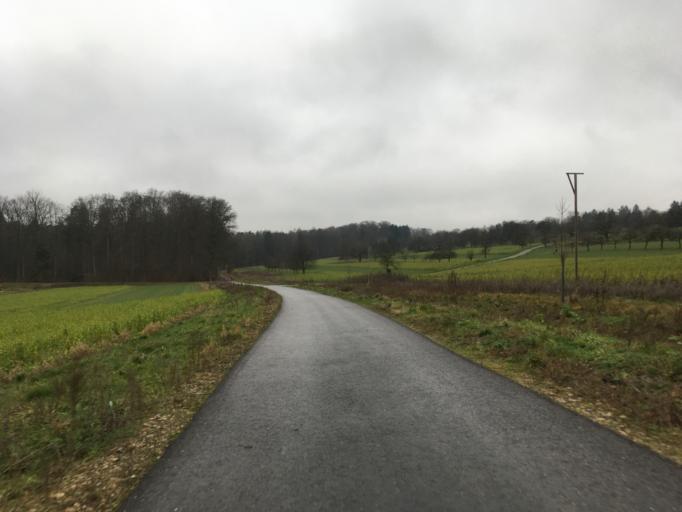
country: DE
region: Baden-Wuerttemberg
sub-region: Karlsruhe Region
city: Konigsbach-Stein
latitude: 48.9477
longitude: 8.5255
